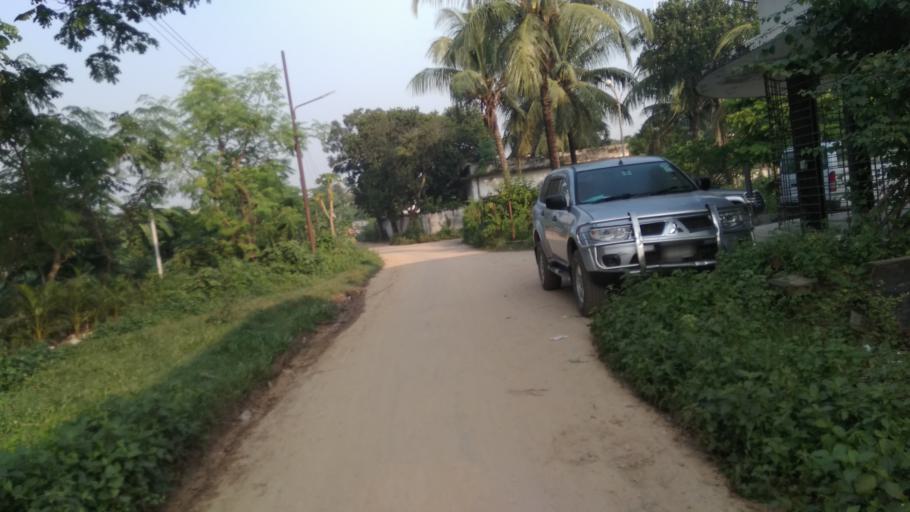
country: BD
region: Dhaka
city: Tungi
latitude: 23.8421
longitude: 90.4195
